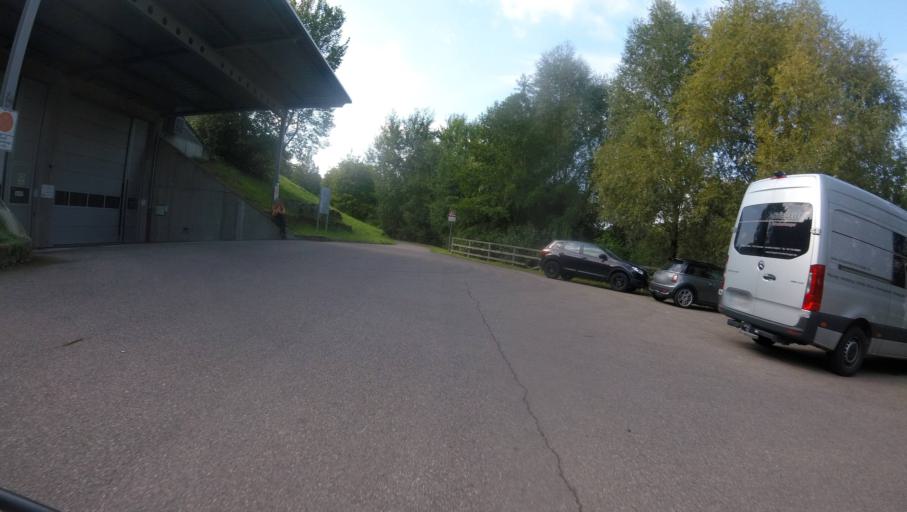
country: DE
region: Baden-Wuerttemberg
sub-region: Regierungsbezirk Stuttgart
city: Stuttgart Muehlhausen
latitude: 48.8421
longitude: 9.2368
